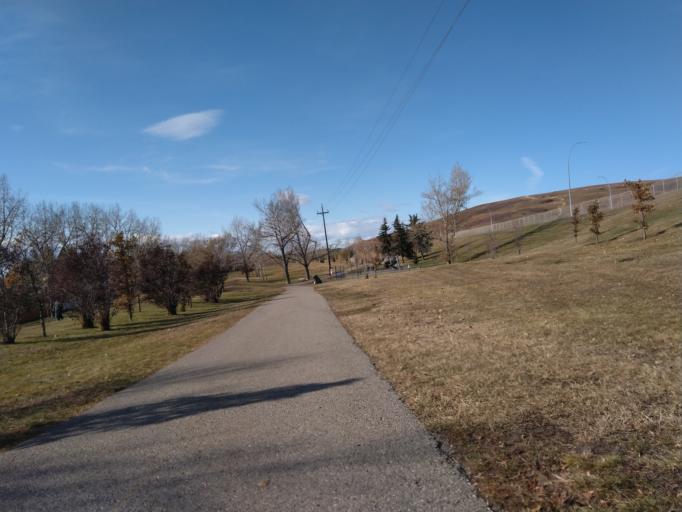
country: CA
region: Alberta
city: Calgary
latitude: 51.0902
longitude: -114.0993
